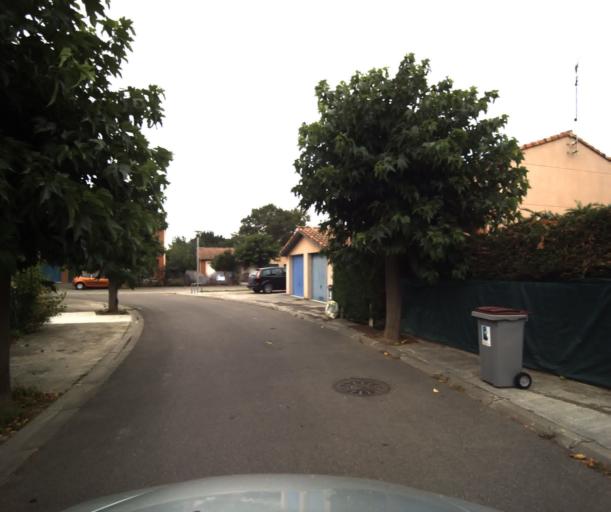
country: FR
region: Midi-Pyrenees
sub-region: Departement de la Haute-Garonne
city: Muret
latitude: 43.4666
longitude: 1.3396
